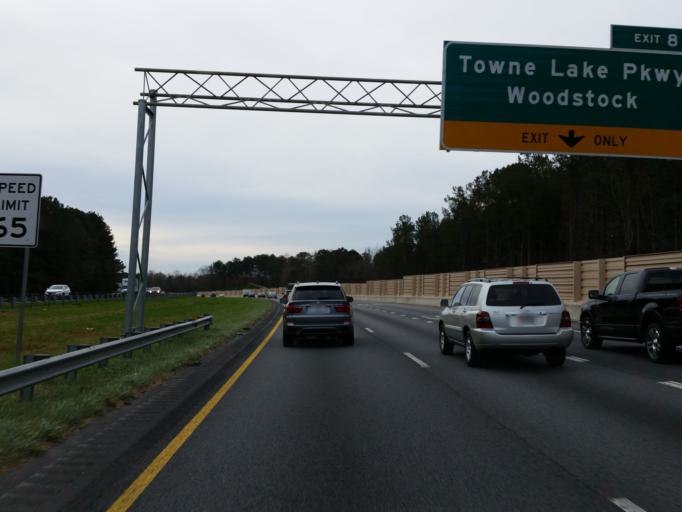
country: US
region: Georgia
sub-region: Cherokee County
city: Woodstock
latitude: 34.1140
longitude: -84.5338
